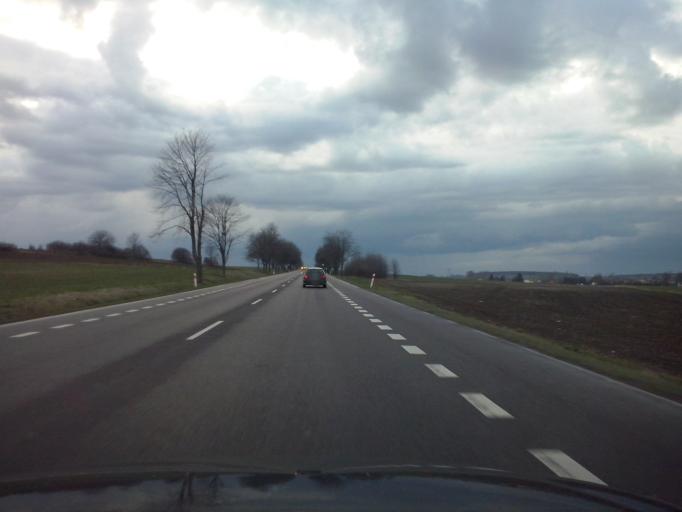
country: PL
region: Lublin Voivodeship
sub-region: Chelm
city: Chelm
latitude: 51.1666
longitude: 23.3666
